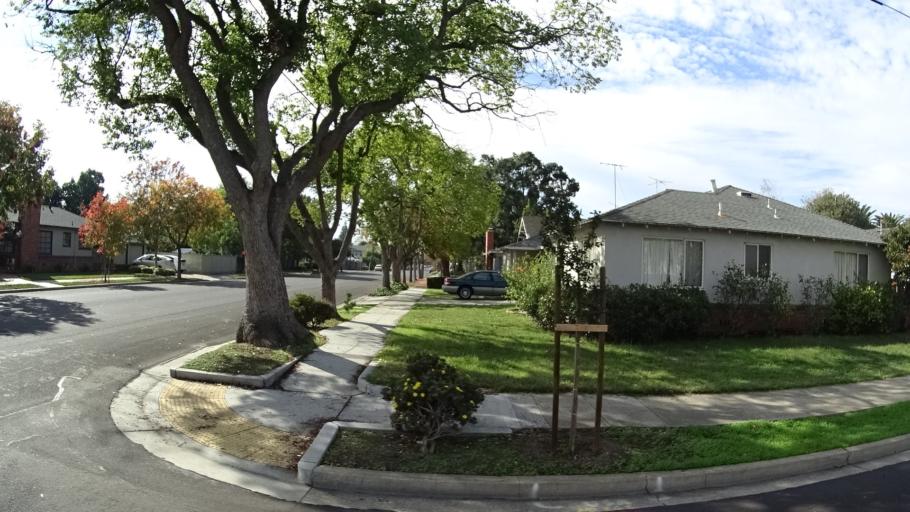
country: US
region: California
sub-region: Santa Clara County
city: Santa Clara
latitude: 37.3518
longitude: -121.9457
